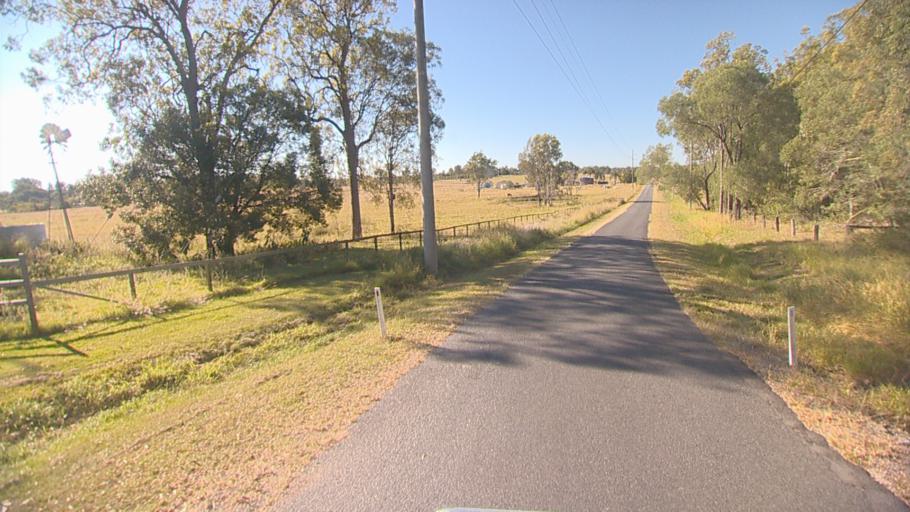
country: AU
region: Queensland
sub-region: Logan
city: Chambers Flat
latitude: -27.7686
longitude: 153.0603
